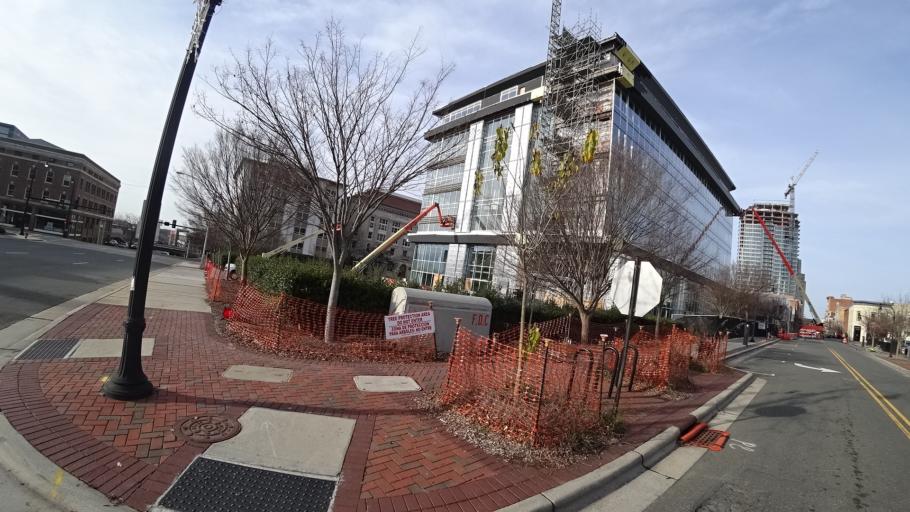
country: US
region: North Carolina
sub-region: Durham County
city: Durham
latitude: 35.9944
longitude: -78.8982
